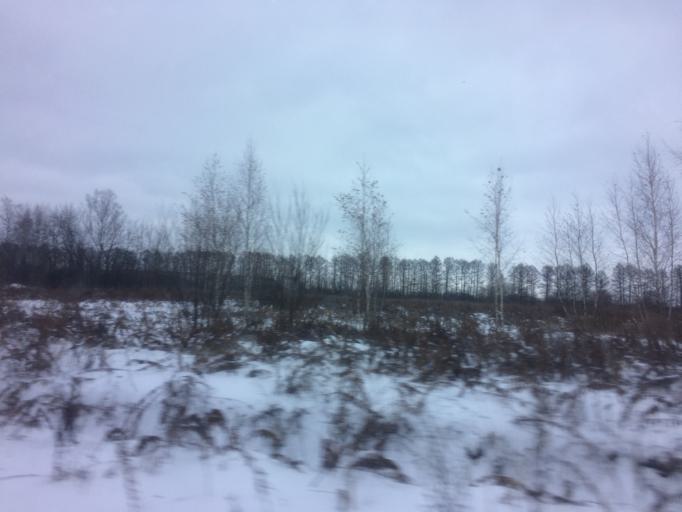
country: RU
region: Tula
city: Mendeleyevskiy
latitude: 54.1396
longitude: 37.6364
